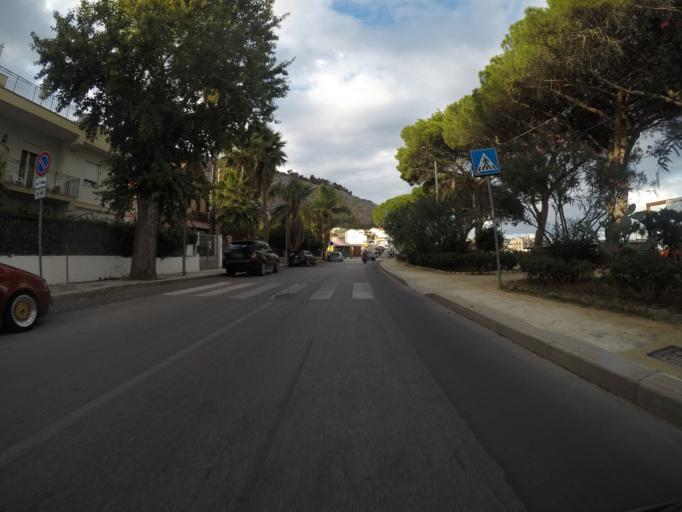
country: IT
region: Sicily
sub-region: Palermo
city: Palermo
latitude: 38.2055
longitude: 13.3250
